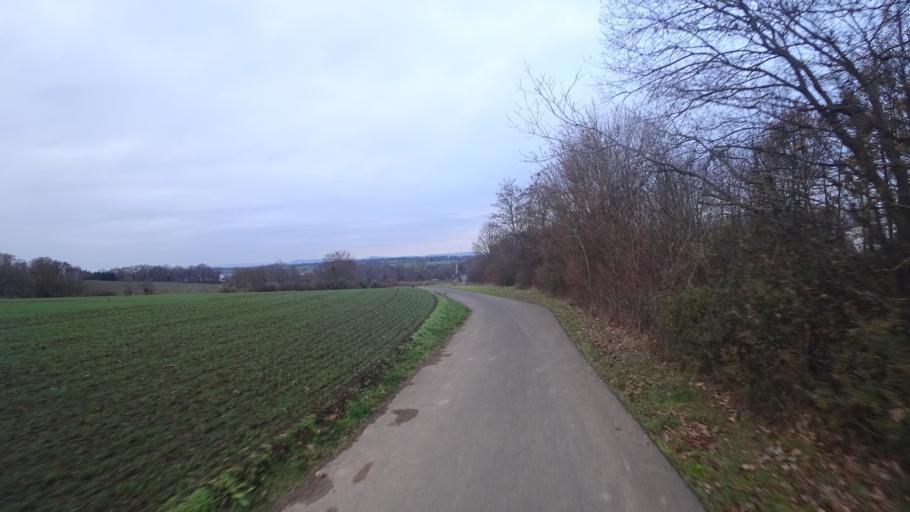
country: DE
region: Rheinland-Pfalz
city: Bassenheim
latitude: 50.3573
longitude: 7.4748
